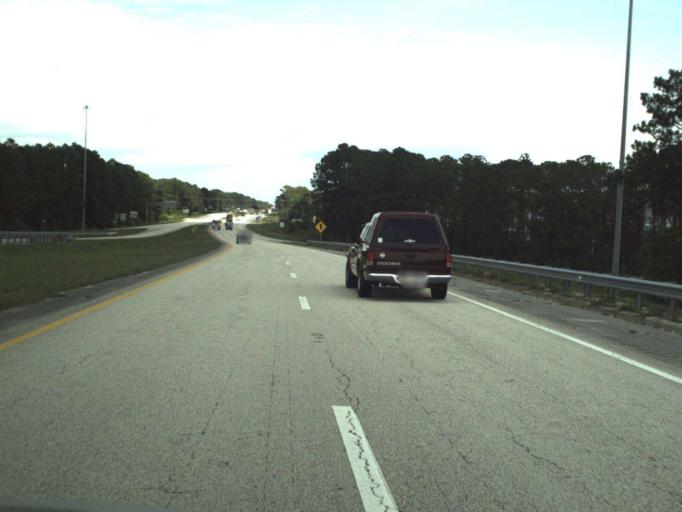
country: US
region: Florida
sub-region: Volusia County
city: South Daytona
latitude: 29.1555
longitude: -81.0751
